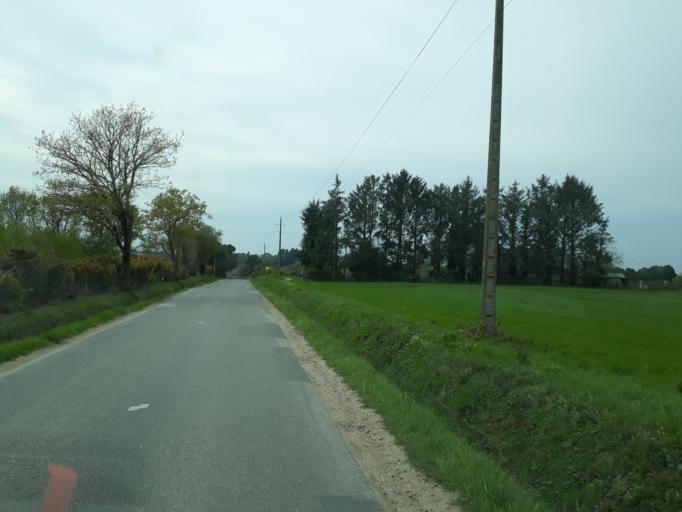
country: FR
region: Brittany
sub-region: Departement du Morbihan
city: Theix
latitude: 47.6385
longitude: -2.6441
